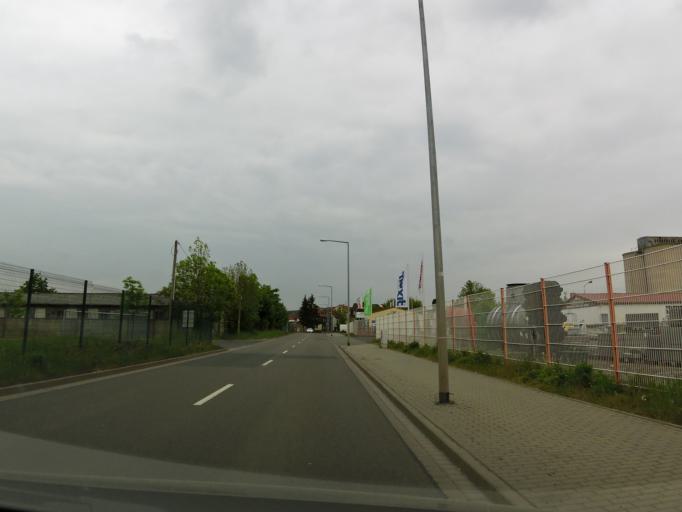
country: DE
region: Thuringia
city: Gotha
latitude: 50.9492
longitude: 10.7275
